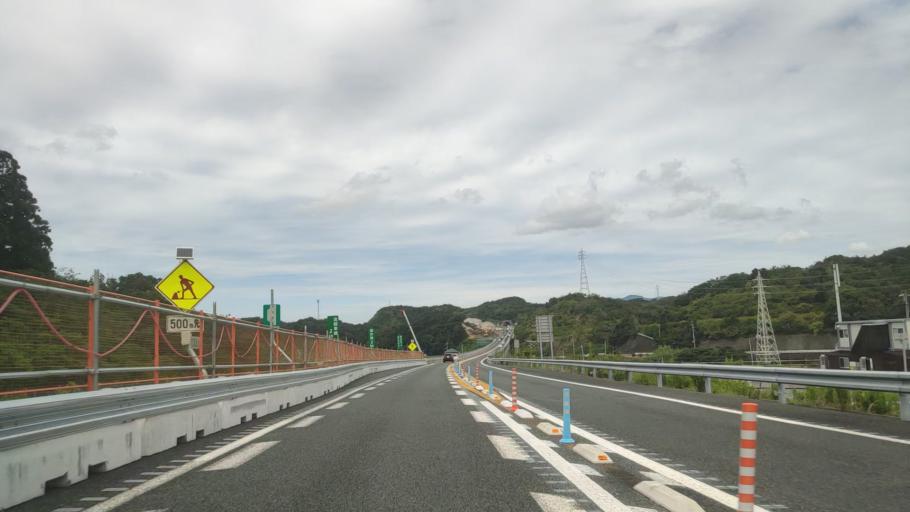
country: JP
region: Wakayama
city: Gobo
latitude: 33.8669
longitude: 135.1904
